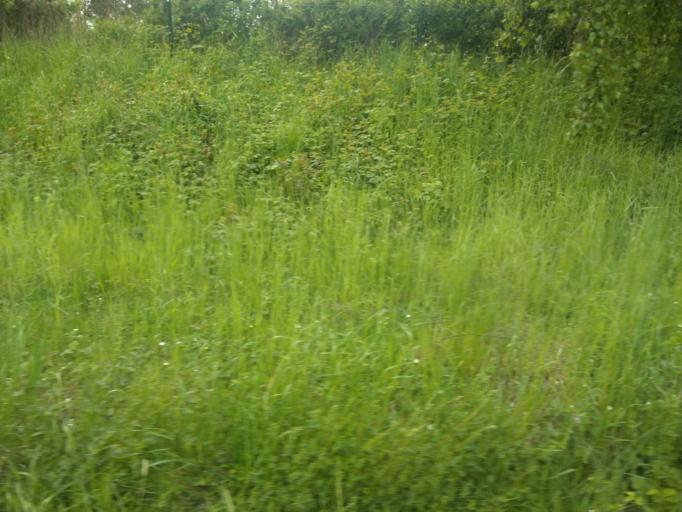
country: SE
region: Stockholm
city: Stenhamra
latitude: 59.4094
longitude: 17.6227
